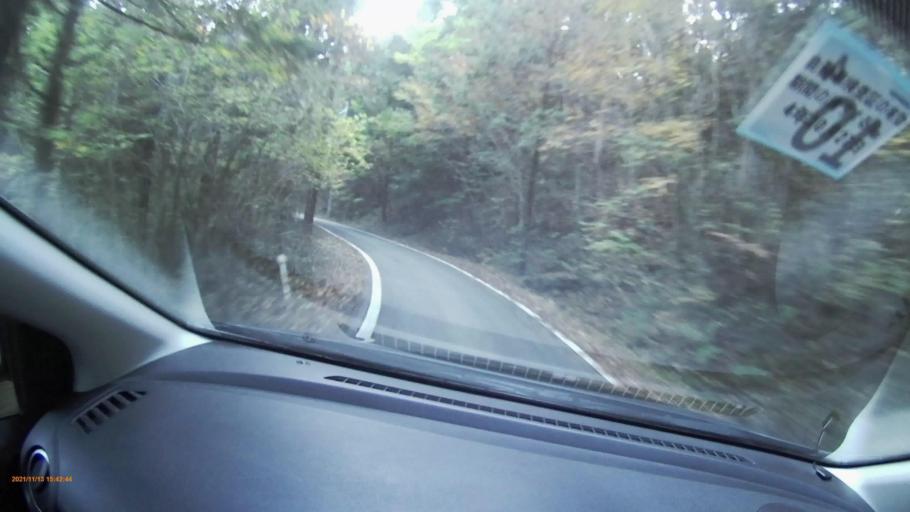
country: JP
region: Gifu
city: Nakatsugawa
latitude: 35.5924
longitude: 137.3925
